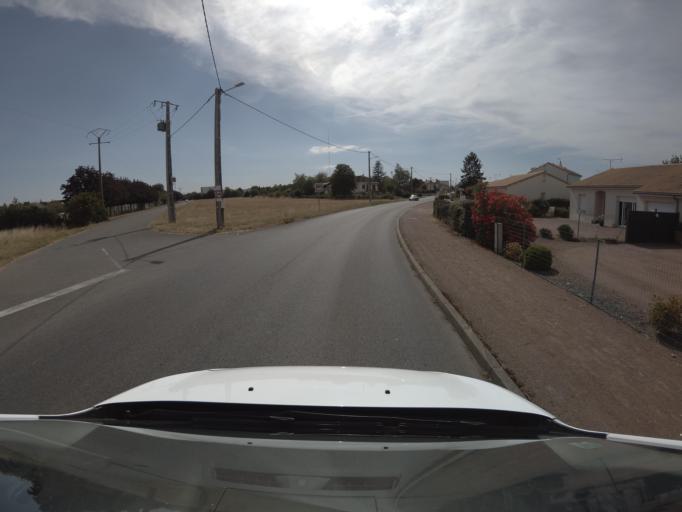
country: FR
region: Poitou-Charentes
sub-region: Departement des Deux-Sevres
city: Thouars
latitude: 46.9800
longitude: -0.1937
